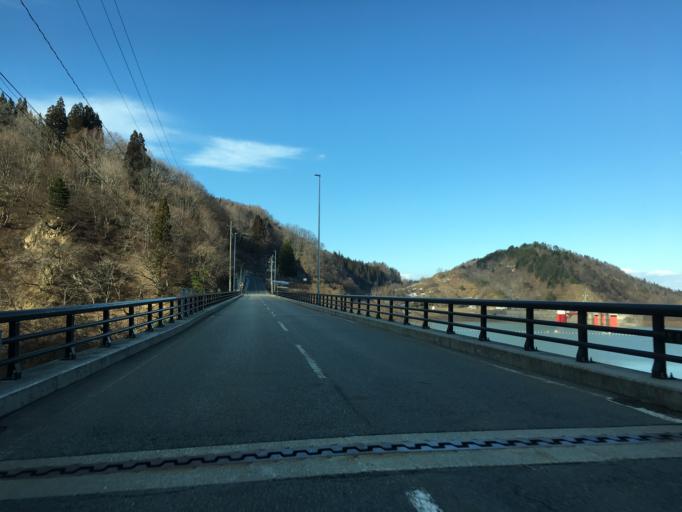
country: JP
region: Yamagata
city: Nagai
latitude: 37.9693
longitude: 139.9155
